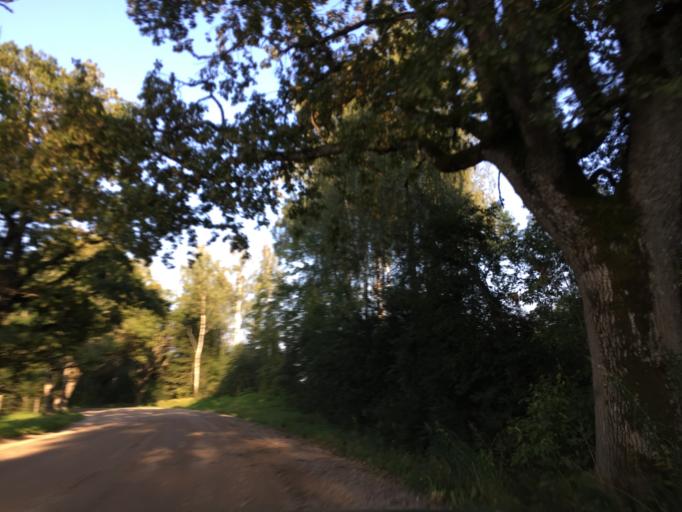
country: LV
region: Limbazu Rajons
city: Limbazi
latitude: 57.5504
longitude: 24.7941
